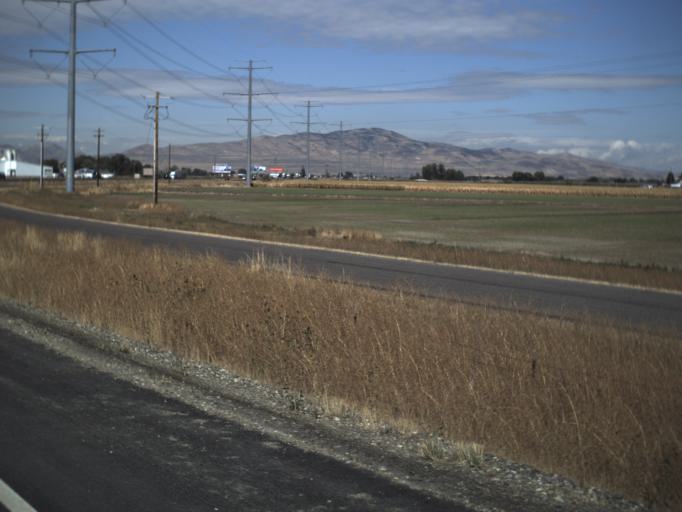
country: US
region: Utah
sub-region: Box Elder County
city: Honeyville
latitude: 41.6359
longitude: -112.0996
